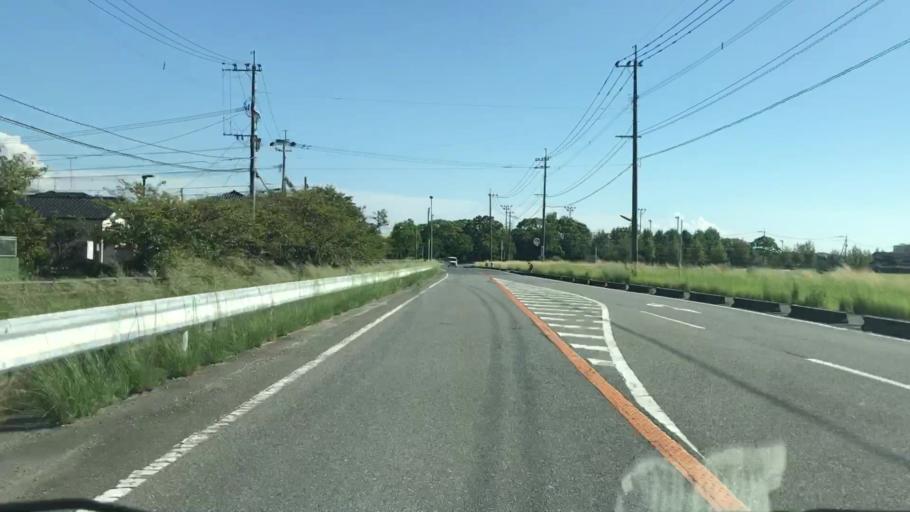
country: JP
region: Saga Prefecture
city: Okawa
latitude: 33.2295
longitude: 130.3558
